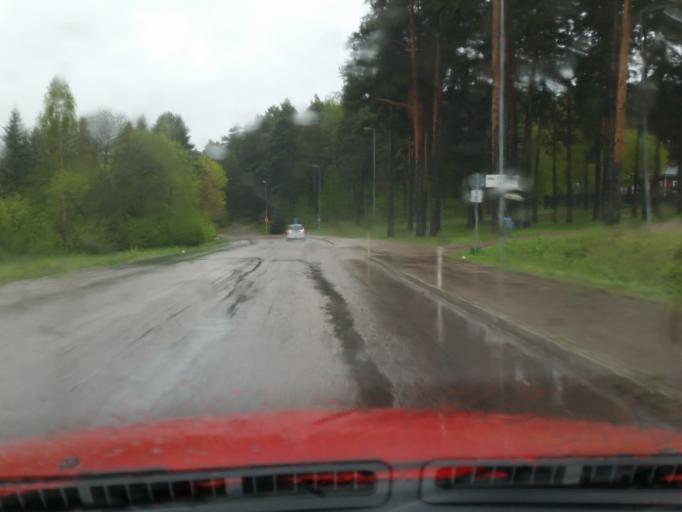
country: SE
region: Dalarna
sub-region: Hedemora Kommun
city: Hedemora
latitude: 60.2927
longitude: 15.9756
